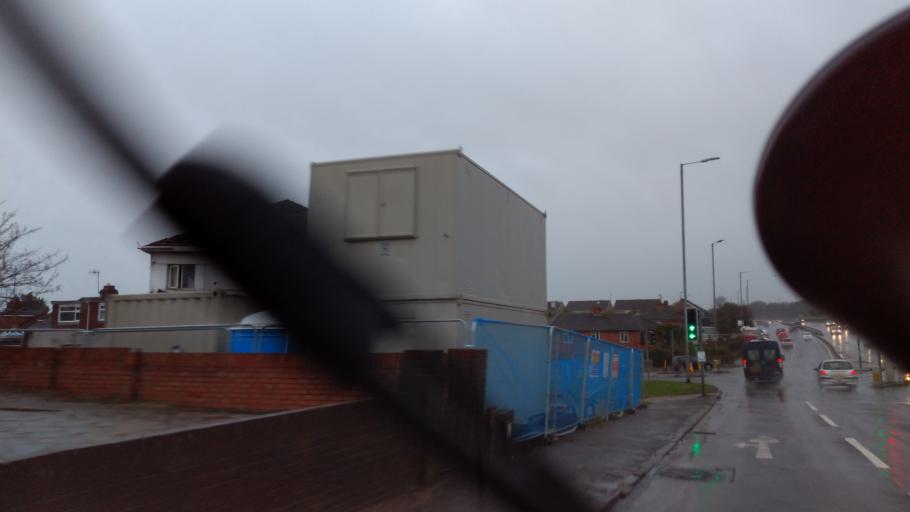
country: GB
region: England
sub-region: West Sussex
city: Lancing
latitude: 50.8375
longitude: -0.3355
